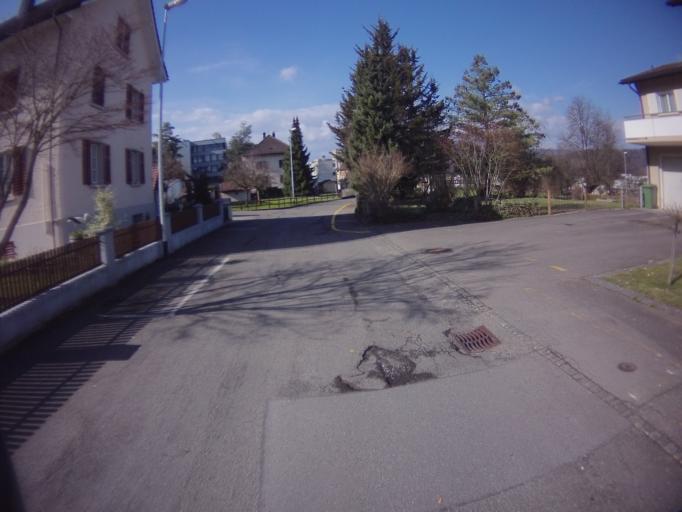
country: CH
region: Aargau
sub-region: Bezirk Baden
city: Spreitenbach
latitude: 47.4191
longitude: 8.3655
